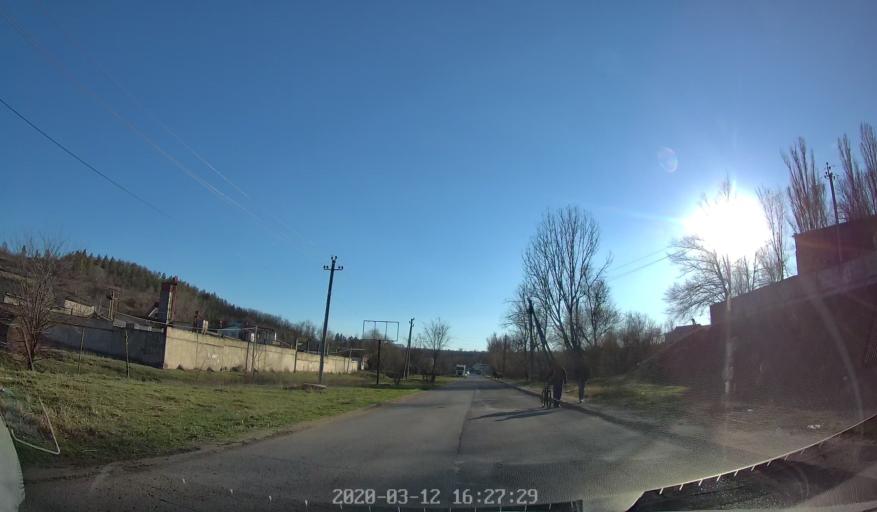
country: MD
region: Anenii Noi
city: Anenii Noi
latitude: 46.8750
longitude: 29.2301
